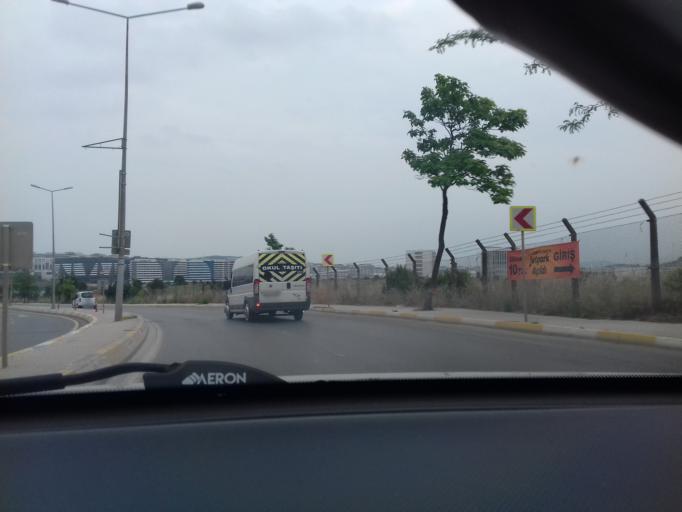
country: TR
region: Istanbul
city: Pendik
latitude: 40.9188
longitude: 29.3081
